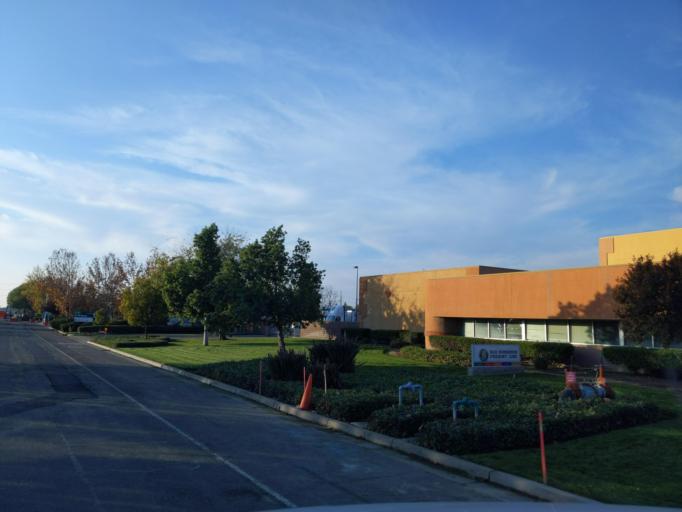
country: US
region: California
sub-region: San Joaquin County
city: Lathrop
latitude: 37.8016
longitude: -121.2892
